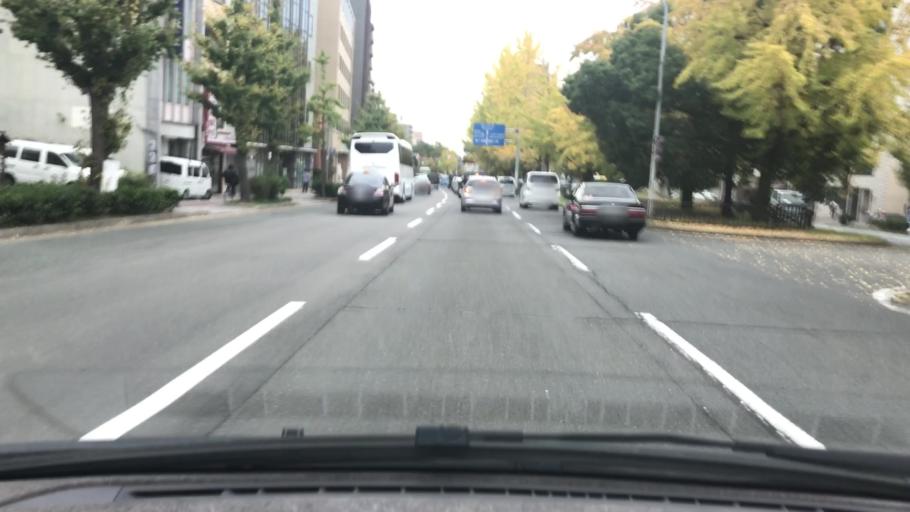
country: JP
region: Kyoto
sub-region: Kyoto-shi
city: Kamigyo-ku
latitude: 35.0316
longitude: 135.7520
